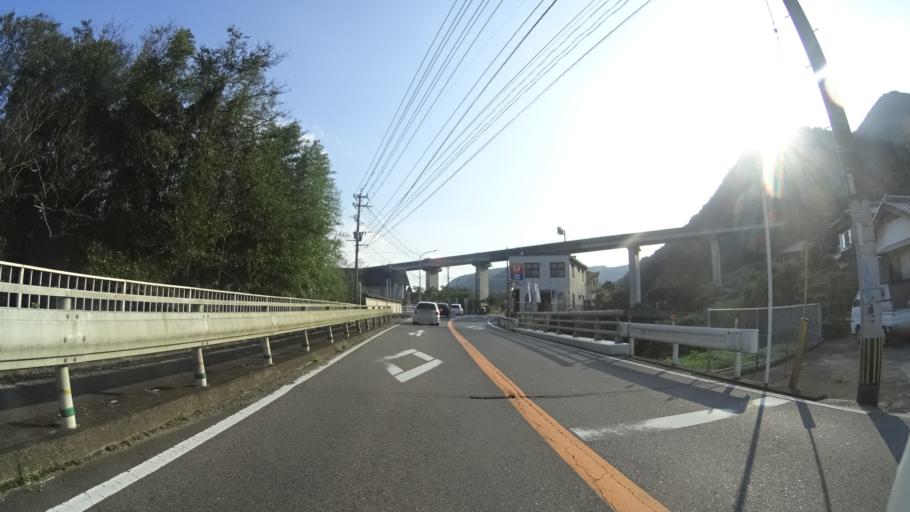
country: JP
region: Oita
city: Bungo-Takada-shi
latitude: 33.4794
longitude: 131.3341
